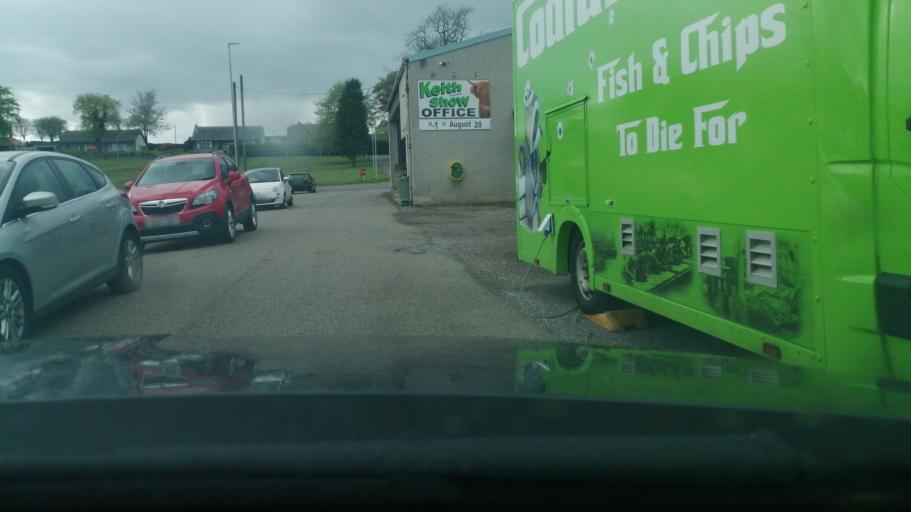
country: GB
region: Scotland
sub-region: Moray
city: Keith
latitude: 57.5361
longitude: -2.9500
